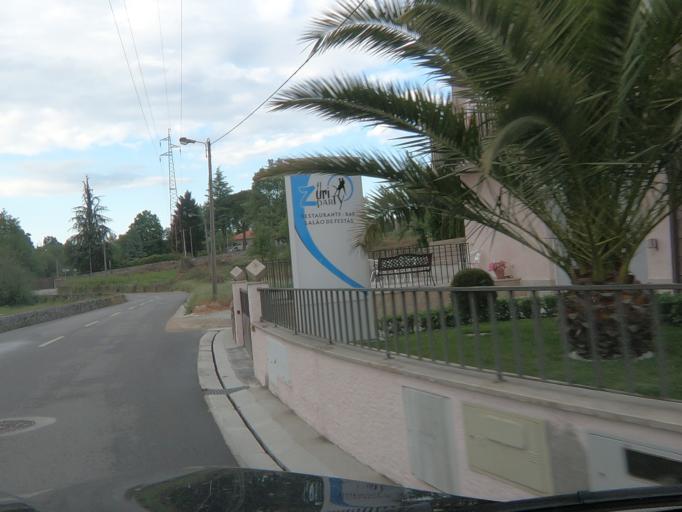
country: PT
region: Vila Real
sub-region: Vila Real
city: Vila Real
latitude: 41.3169
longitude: -7.7426
